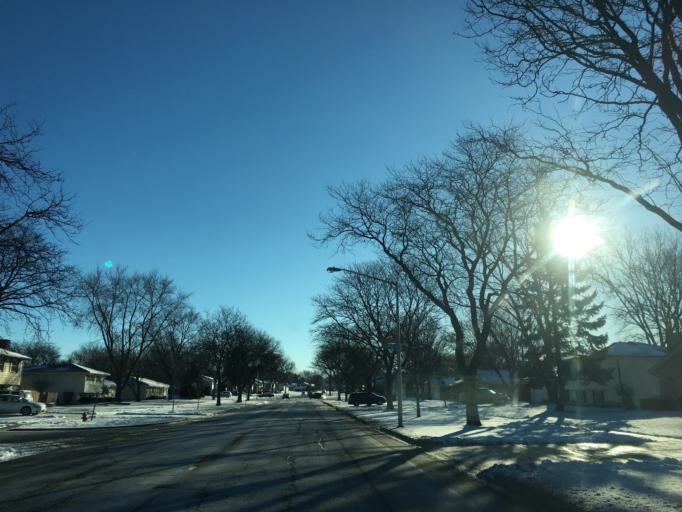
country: US
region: Illinois
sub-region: Cook County
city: Schaumburg
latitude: 42.0178
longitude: -88.1014
